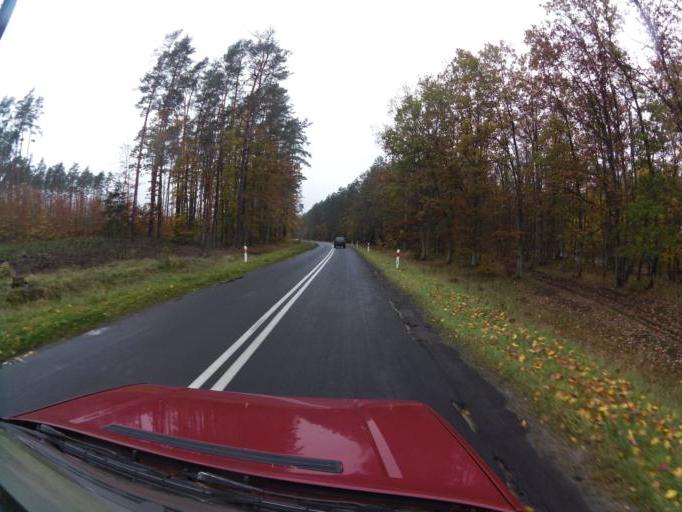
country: PL
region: West Pomeranian Voivodeship
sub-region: Powiat policki
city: Dobra
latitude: 53.5808
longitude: 14.4235
